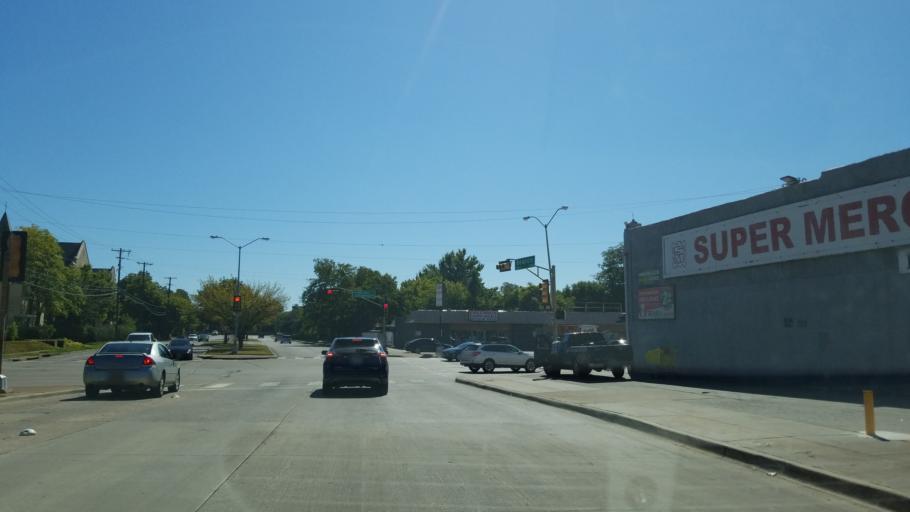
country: US
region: Texas
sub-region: Dallas County
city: Highland Park
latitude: 32.8014
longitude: -96.7568
